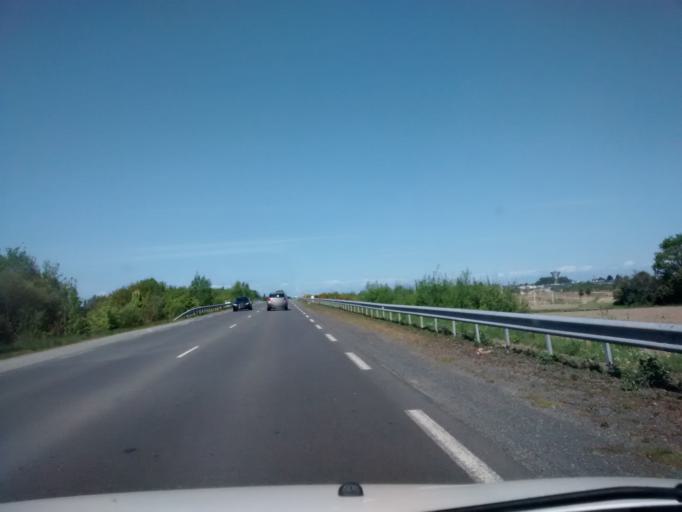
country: FR
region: Brittany
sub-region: Departement d'Ille-et-Vilaine
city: Dinard
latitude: 48.6048
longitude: -2.0684
